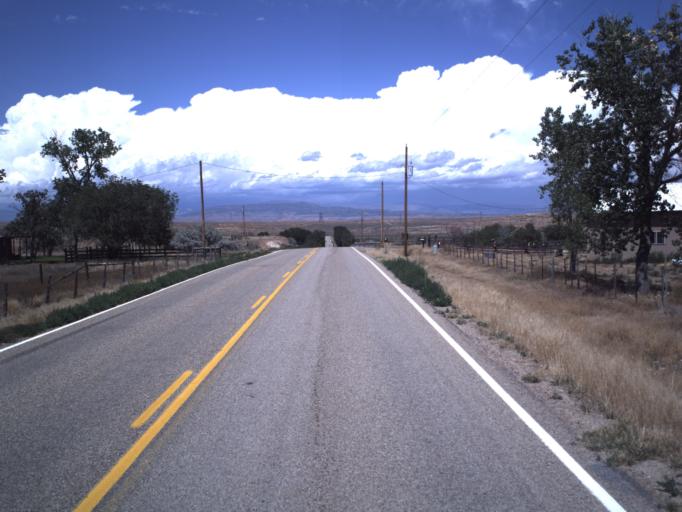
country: US
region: Utah
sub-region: Uintah County
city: Maeser
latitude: 40.2441
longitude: -109.6843
